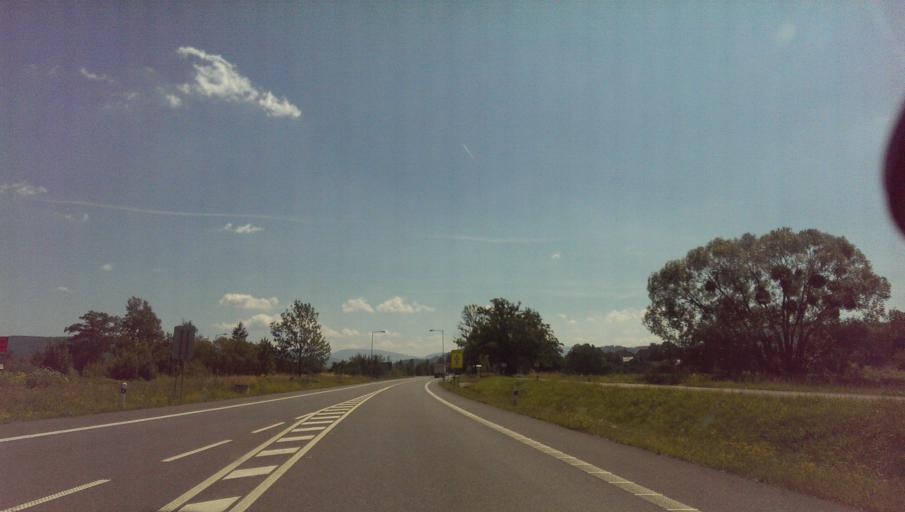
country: CZ
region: Moravskoslezsky
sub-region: Okres Novy Jicin
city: Pribor
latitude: 49.6207
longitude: 18.1511
